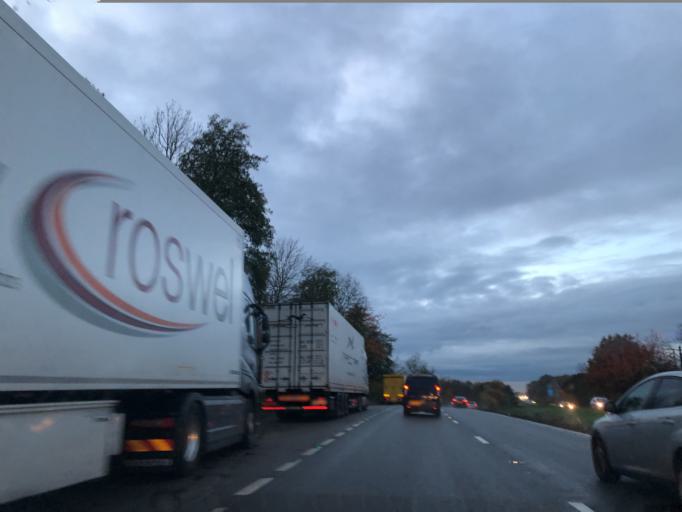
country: GB
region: England
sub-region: Solihull
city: Hampton in Arden
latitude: 52.4475
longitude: -1.6890
